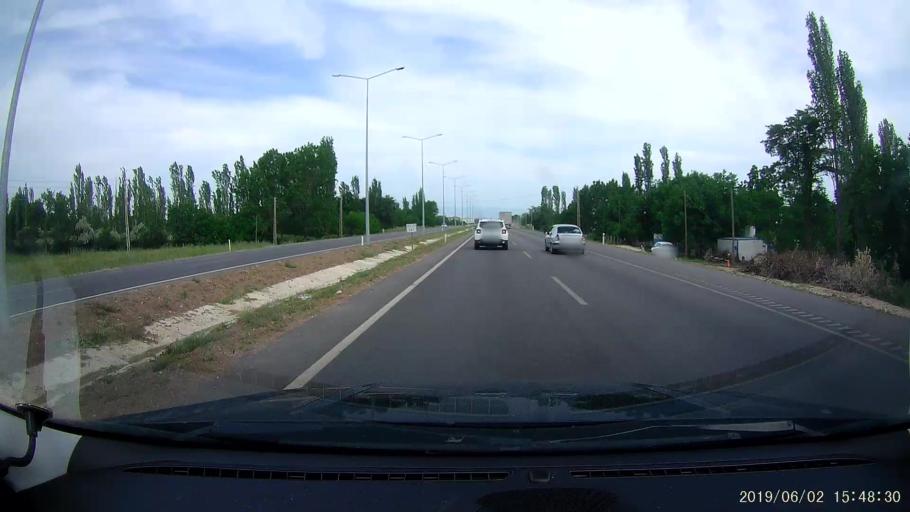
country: TR
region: Amasya
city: Merzifon
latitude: 40.8622
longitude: 35.4430
